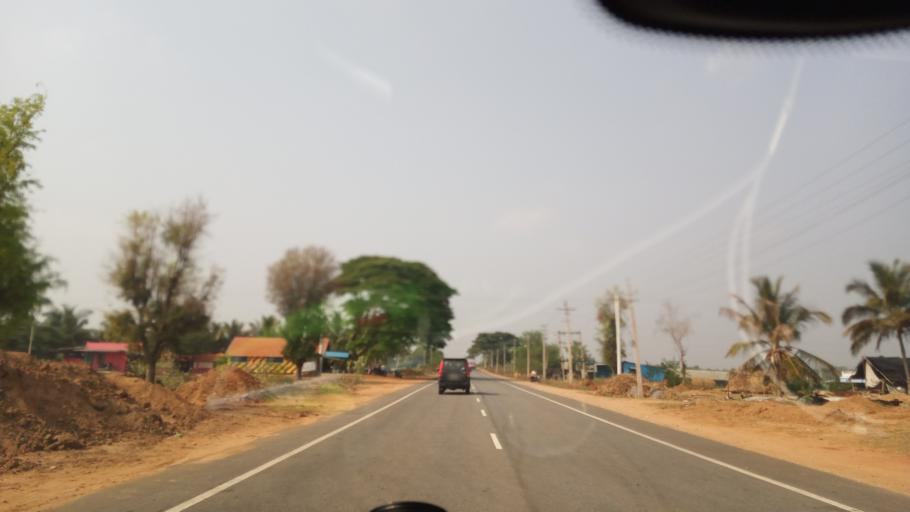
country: IN
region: Karnataka
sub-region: Mandya
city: Nagamangala
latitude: 12.7482
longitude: 76.7275
